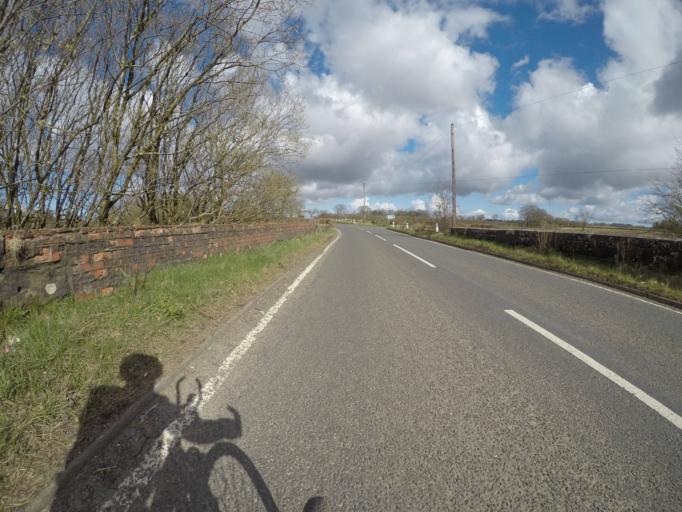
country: GB
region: Scotland
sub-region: North Ayrshire
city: Beith
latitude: 55.7350
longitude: -4.6168
